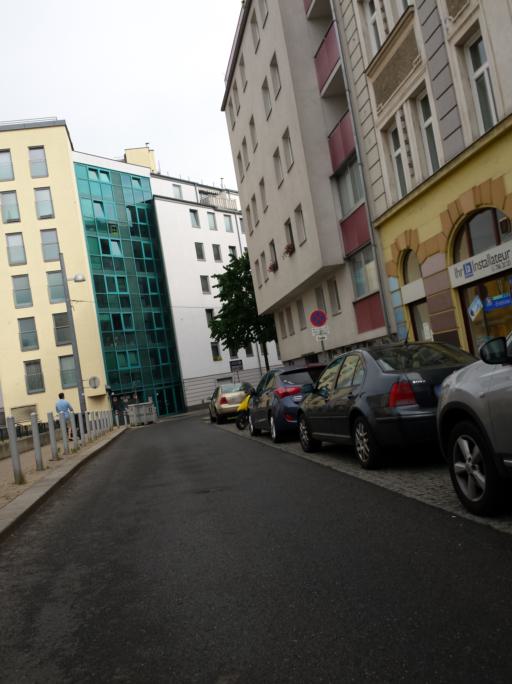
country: AT
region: Vienna
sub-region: Wien Stadt
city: Vienna
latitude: 48.2001
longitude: 16.3108
